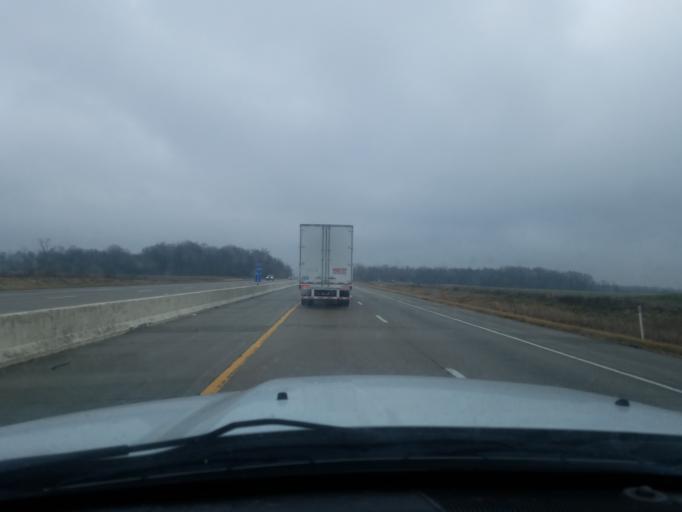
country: US
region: Indiana
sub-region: Wells County
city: Ossian
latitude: 40.9527
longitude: -85.2222
